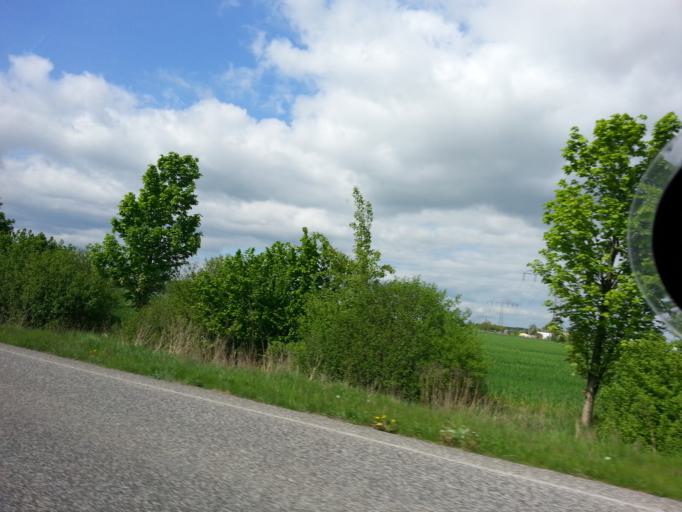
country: DE
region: Brandenburg
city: Werneuchen
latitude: 52.6112
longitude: 13.6650
